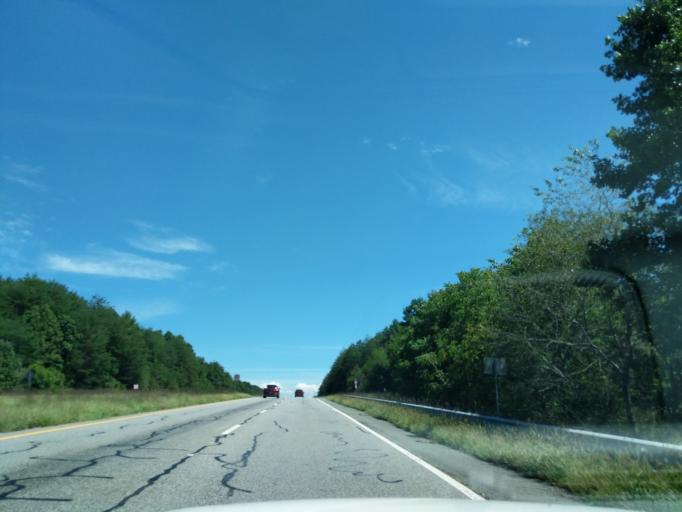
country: US
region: Georgia
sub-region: Fannin County
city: Blue Ridge
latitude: 34.8923
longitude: -84.2455
